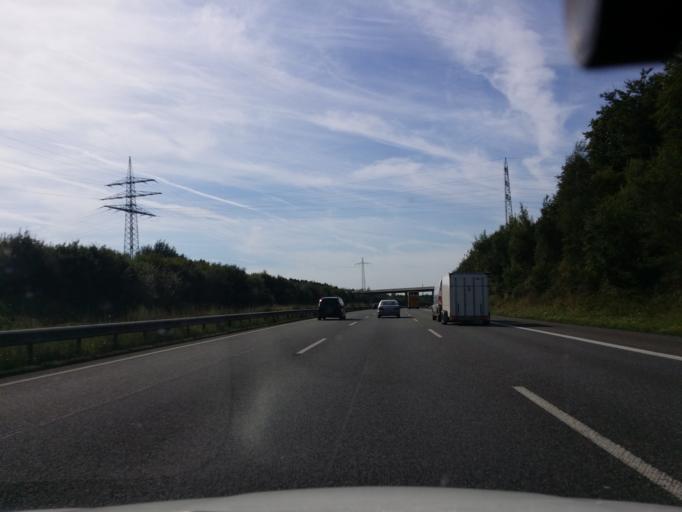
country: DE
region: Rheinland-Pfalz
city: Oberraden
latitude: 50.5593
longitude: 7.5462
